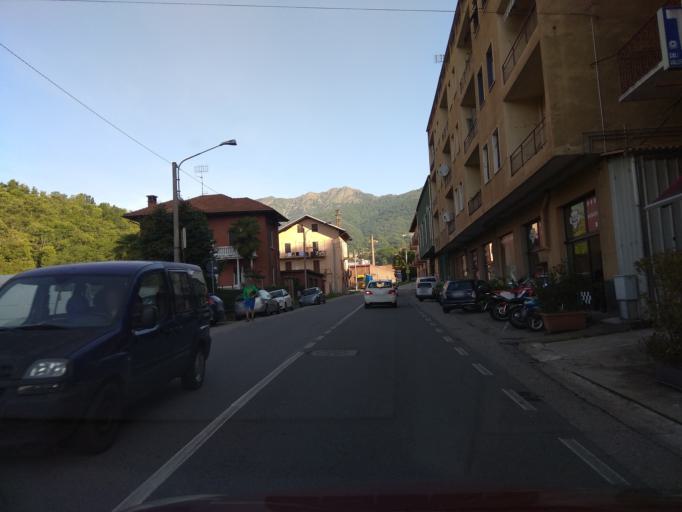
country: IT
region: Piedmont
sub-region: Provincia di Biella
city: Valle Mosso
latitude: 45.6273
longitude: 8.1504
